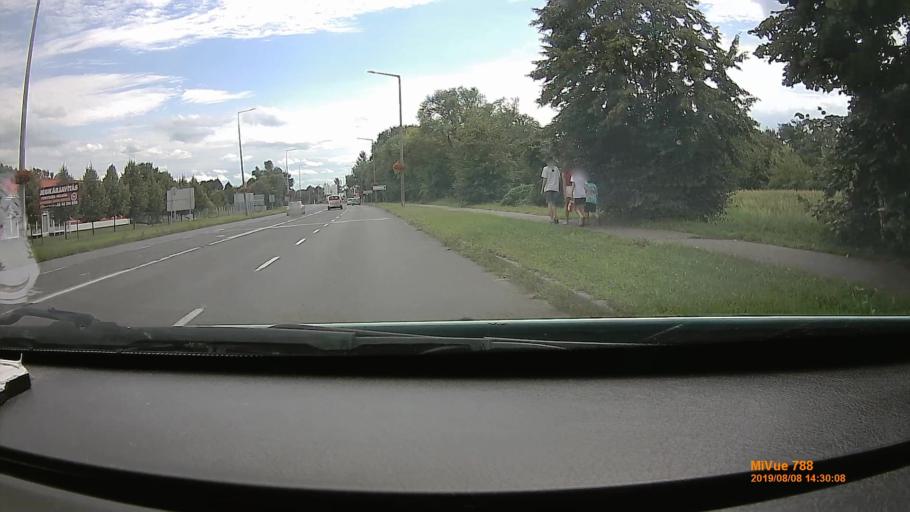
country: HU
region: Szabolcs-Szatmar-Bereg
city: Mateszalka
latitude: 47.9502
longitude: 22.3249
